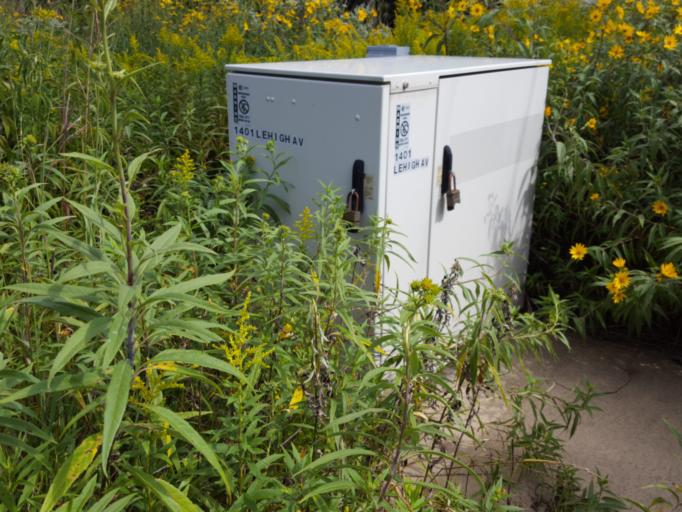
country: US
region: Illinois
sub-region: Cook County
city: Glenview
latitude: 42.0806
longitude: -87.8090
